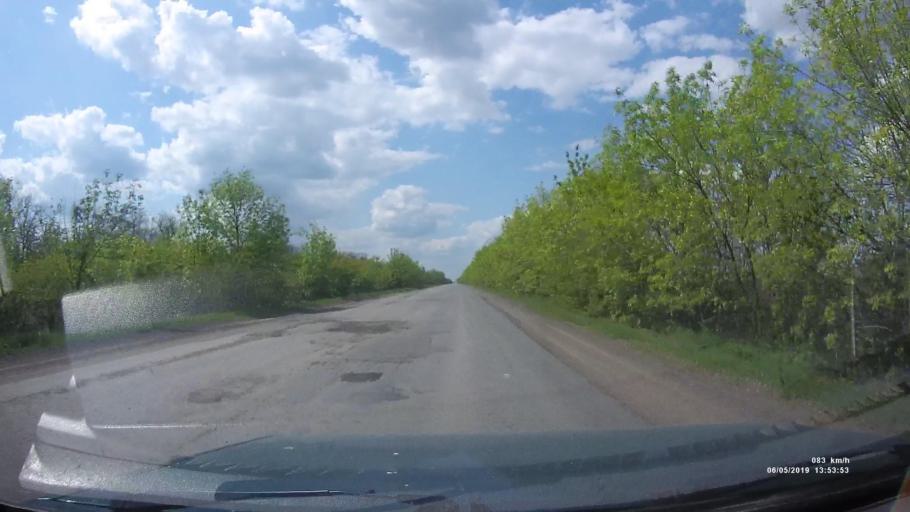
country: RU
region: Rostov
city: Melikhovskaya
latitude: 47.6711
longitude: 40.4556
